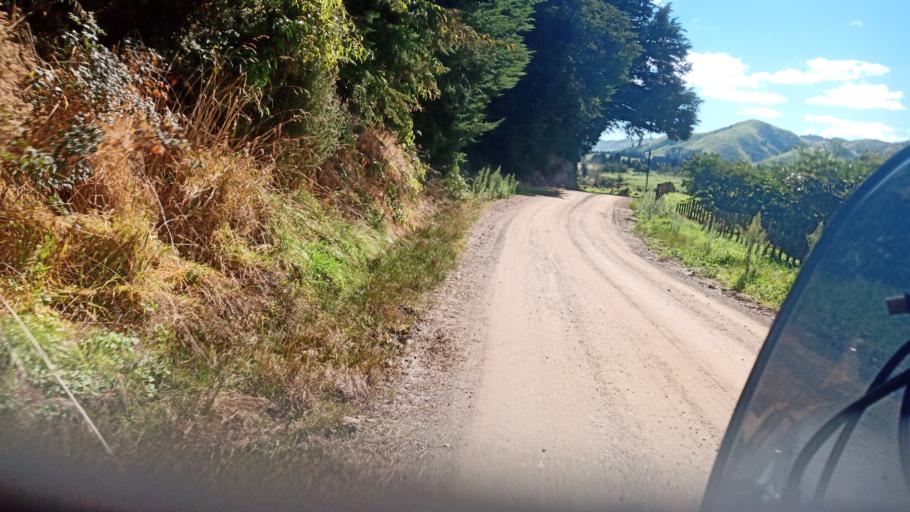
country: NZ
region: Bay of Plenty
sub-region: Opotiki District
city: Opotiki
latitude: -38.3288
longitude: 177.5738
